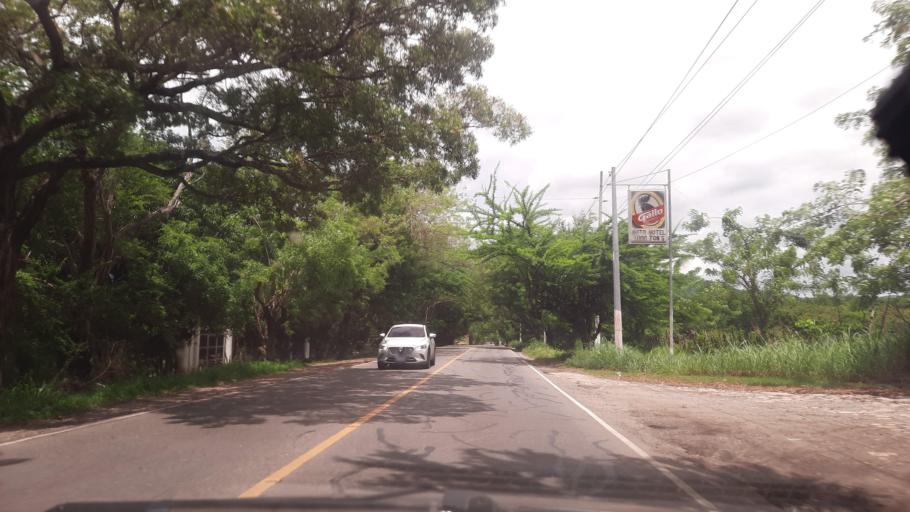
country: GT
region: Zacapa
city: Estanzuela
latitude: 14.9862
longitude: -89.5613
